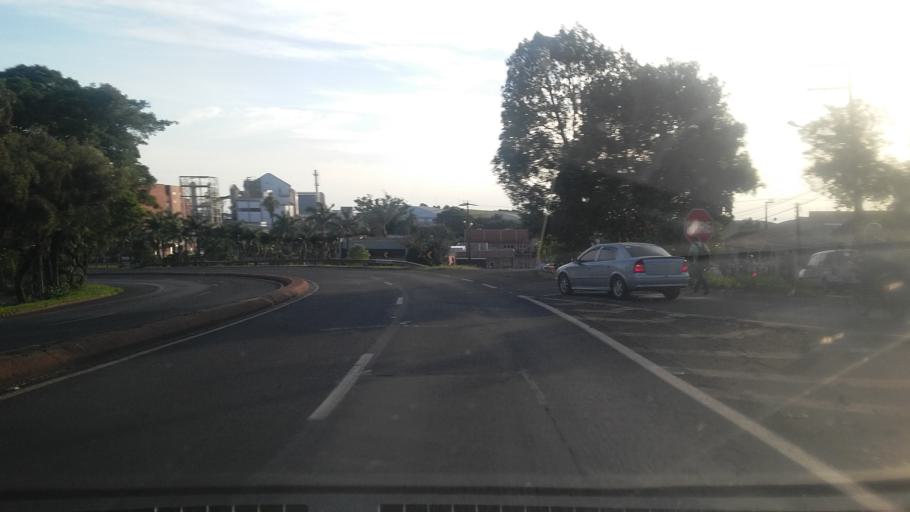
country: BR
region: Parana
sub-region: Assai
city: Assai
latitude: -23.1885
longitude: -50.6404
